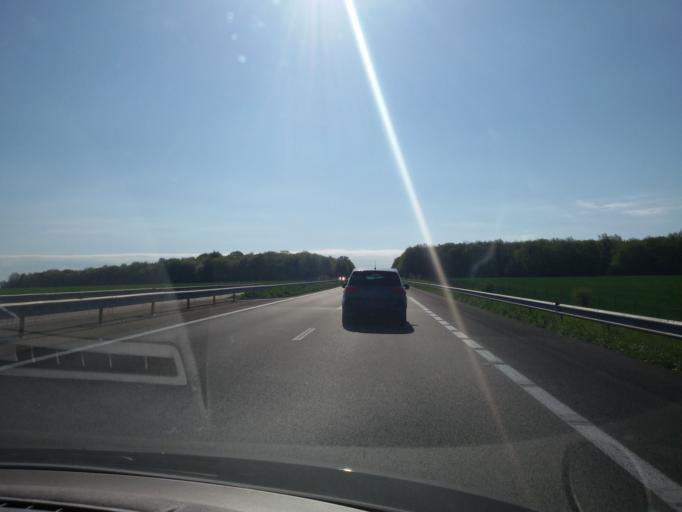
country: FR
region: Bourgogne
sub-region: Departement de l'Yonne
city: Vermenton
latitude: 47.7133
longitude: 3.7757
